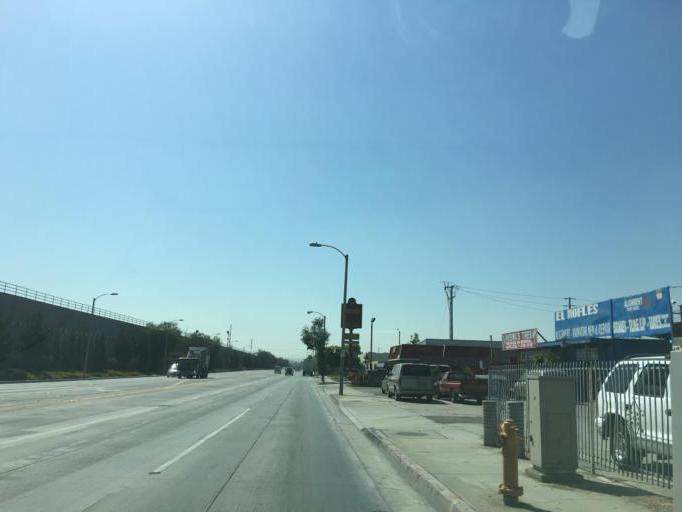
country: US
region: California
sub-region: Los Angeles County
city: Avocado Heights
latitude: 34.0379
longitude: -117.9794
